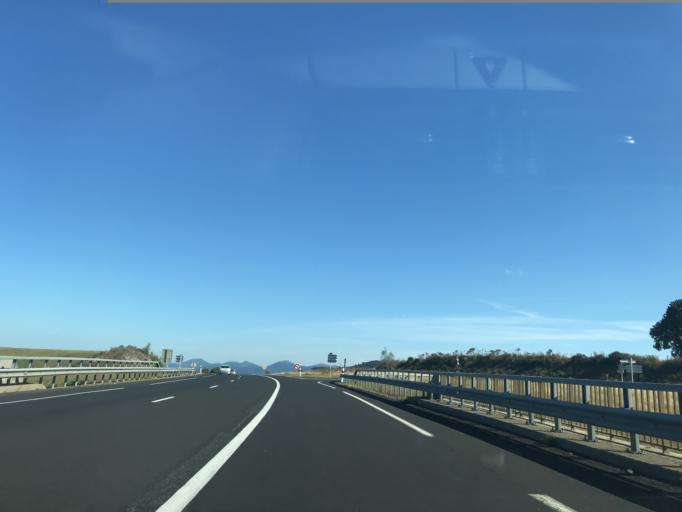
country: FR
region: Auvergne
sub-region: Departement du Puy-de-Dome
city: La Bourboule
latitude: 45.6668
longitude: 2.7840
